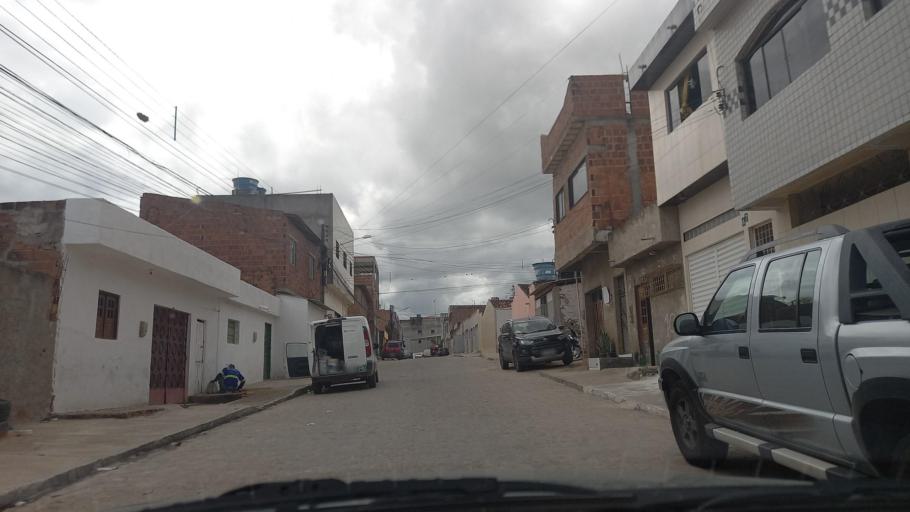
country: BR
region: Pernambuco
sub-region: Caruaru
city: Caruaru
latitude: -8.2669
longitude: -35.9567
